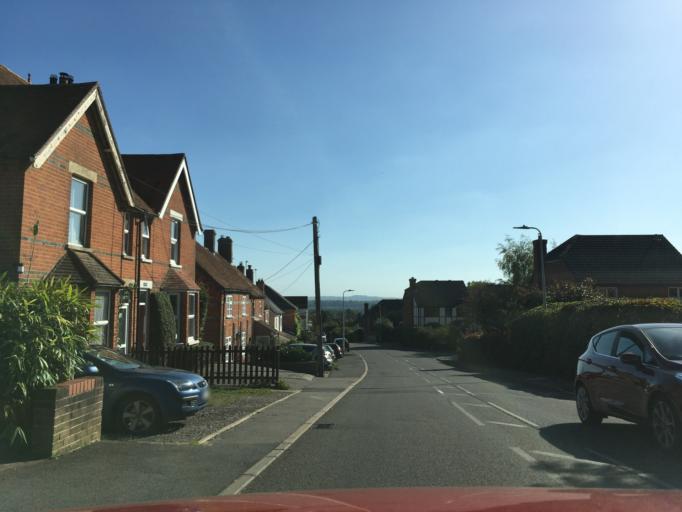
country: GB
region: England
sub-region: West Berkshire
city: Cold Ash
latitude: 51.4224
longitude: -1.2645
